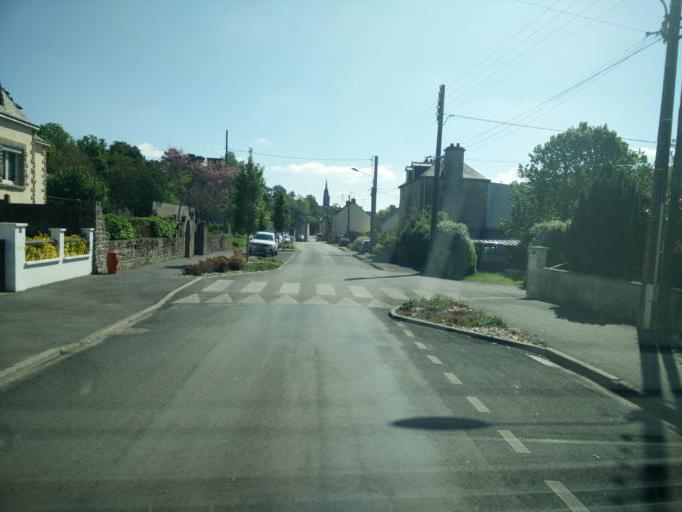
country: FR
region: Brittany
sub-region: Departement du Morbihan
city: Josselin
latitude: 47.9530
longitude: -2.5578
